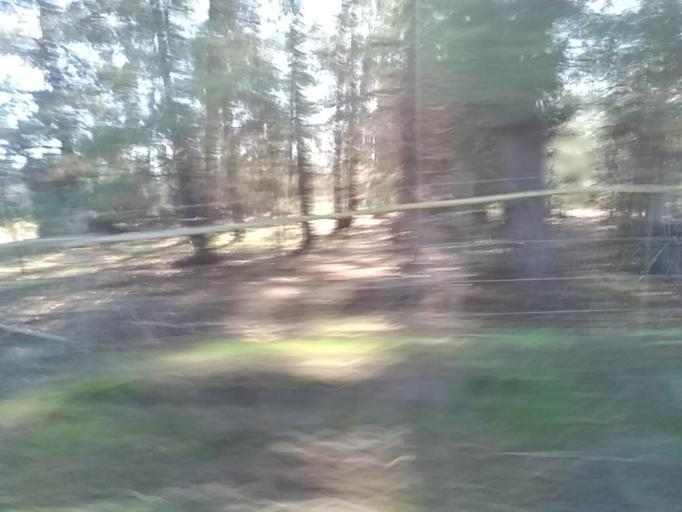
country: CL
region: Valparaiso
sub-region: San Antonio Province
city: El Tabo
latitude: -33.4121
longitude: -71.6085
